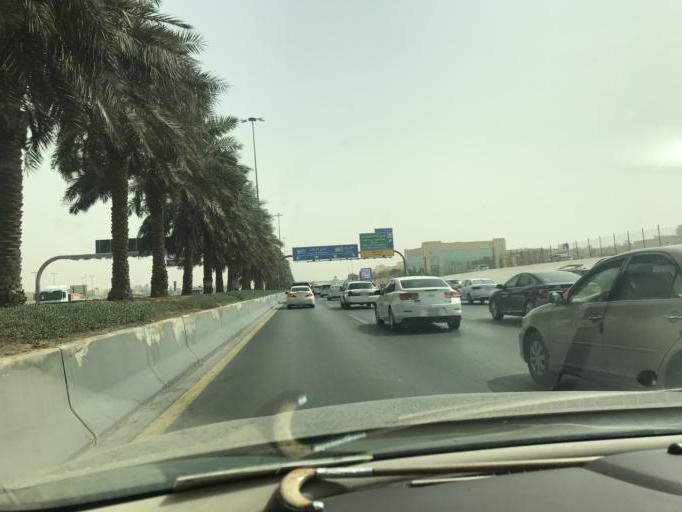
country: SA
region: Ar Riyad
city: Riyadh
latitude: 24.7823
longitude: 46.7268
